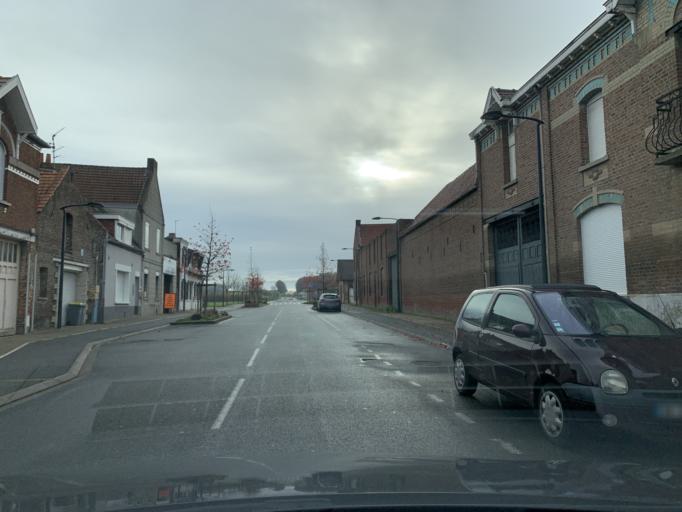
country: FR
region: Nord-Pas-de-Calais
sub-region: Departement du Nord
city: Cantin
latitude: 50.3084
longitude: 3.1289
